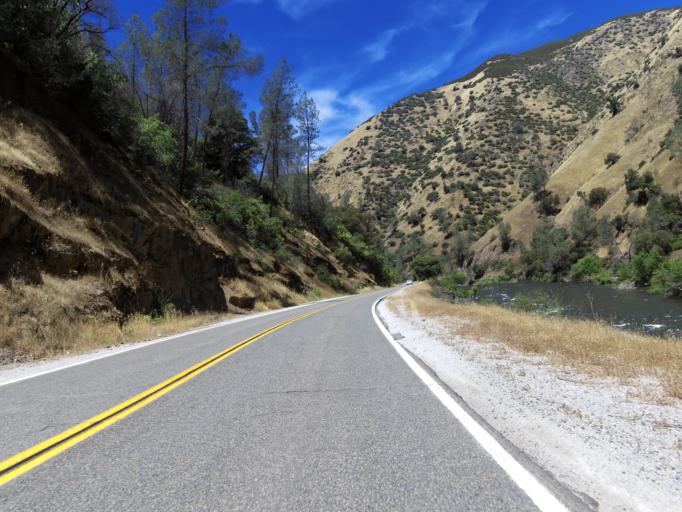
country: US
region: California
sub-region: Mariposa County
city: Midpines
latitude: 37.6310
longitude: -119.9405
